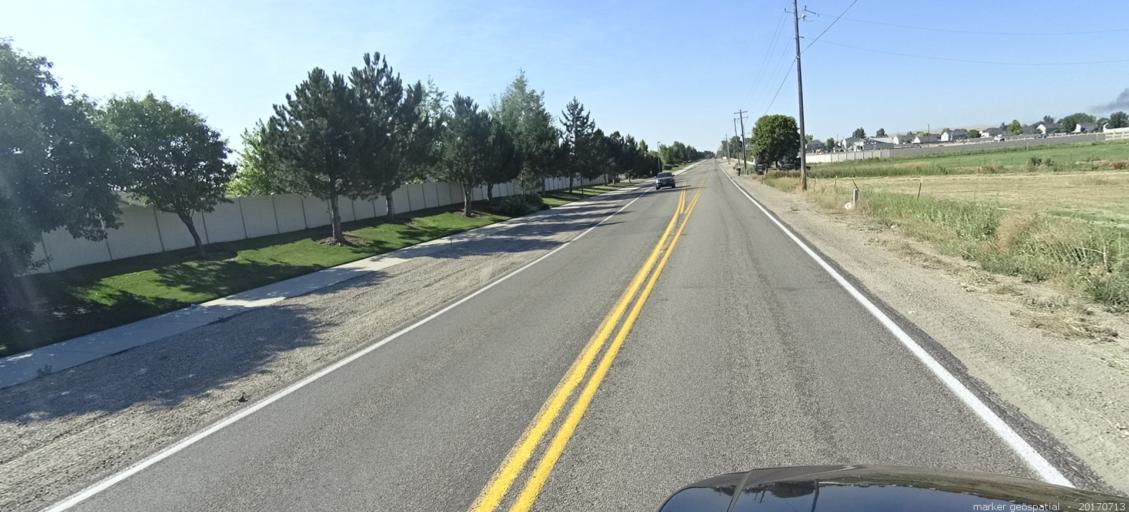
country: US
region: Idaho
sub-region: Ada County
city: Kuna
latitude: 43.5113
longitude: -116.4138
